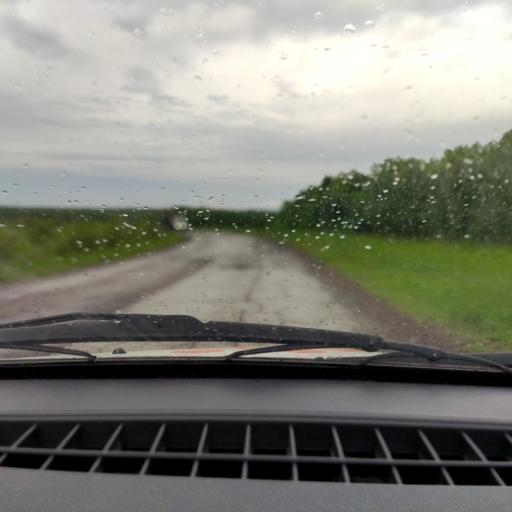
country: RU
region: Bashkortostan
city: Kudeyevskiy
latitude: 54.8502
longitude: 56.8051
